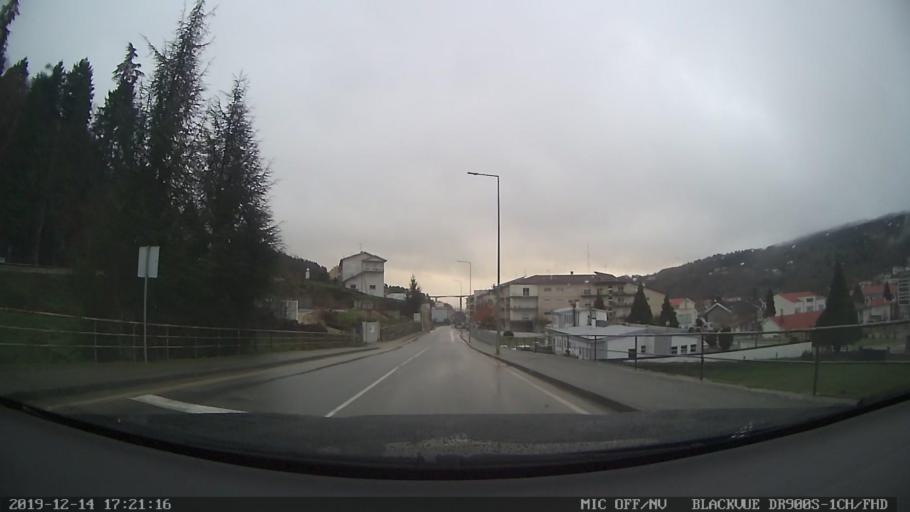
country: PT
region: Vila Real
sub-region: Vila Pouca de Aguiar
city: Vila Pouca de Aguiar
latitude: 41.4989
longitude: -7.6410
